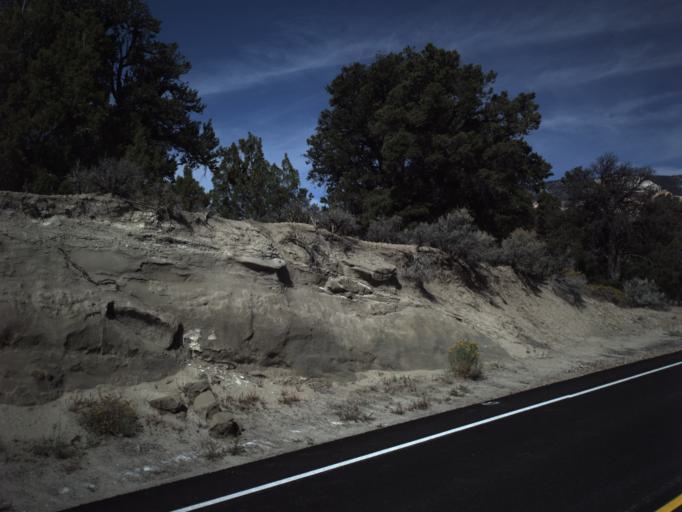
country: US
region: Utah
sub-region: Garfield County
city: Panguitch
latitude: 37.6385
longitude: -111.8437
